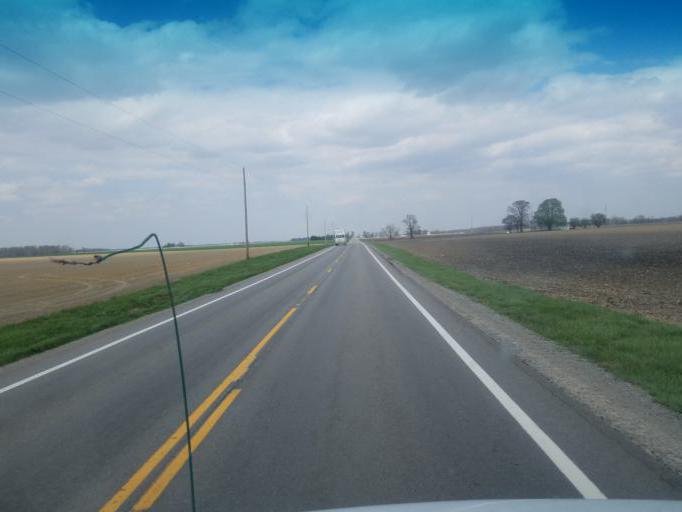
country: US
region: Ohio
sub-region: Wyandot County
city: Upper Sandusky
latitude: 40.8885
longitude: -83.2765
